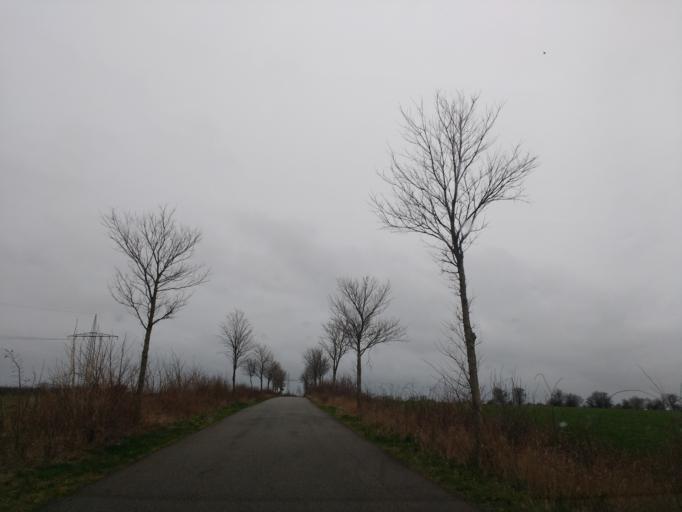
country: DE
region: Schleswig-Holstein
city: Grossenbrode
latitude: 54.3861
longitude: 11.1077
